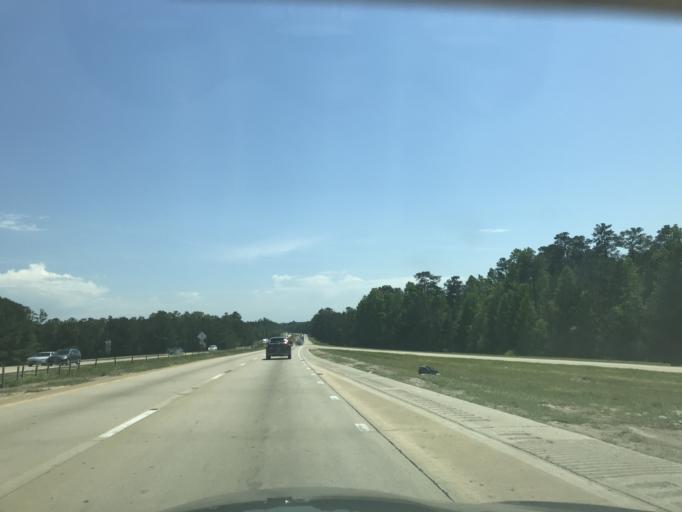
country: US
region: North Carolina
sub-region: Wake County
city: Garner
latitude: 35.6938
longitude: -78.5745
